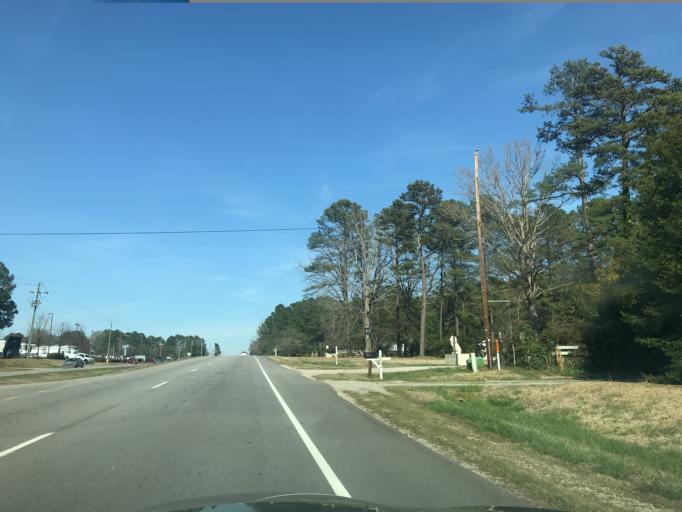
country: US
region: North Carolina
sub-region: Wake County
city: Fuquay-Varina
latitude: 35.6217
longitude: -78.7276
